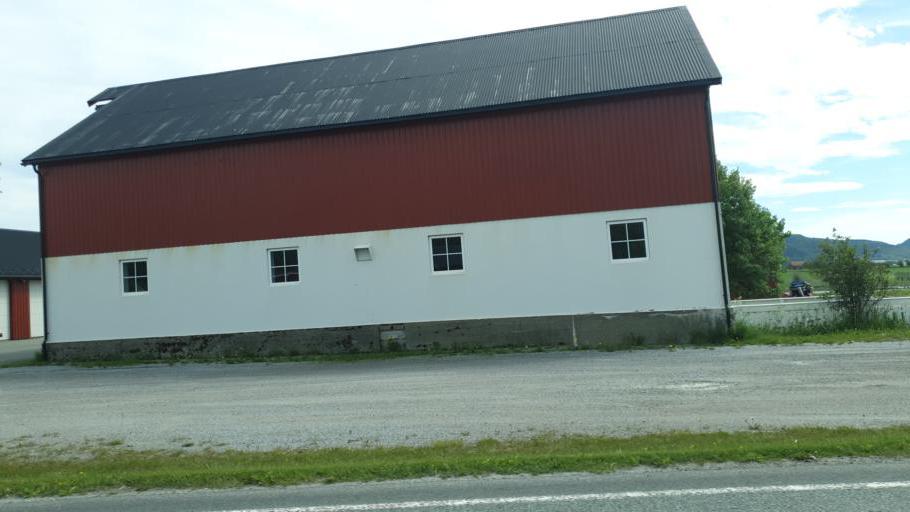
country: NO
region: Sor-Trondelag
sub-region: Rissa
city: Rissa
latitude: 63.5812
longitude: 9.9421
